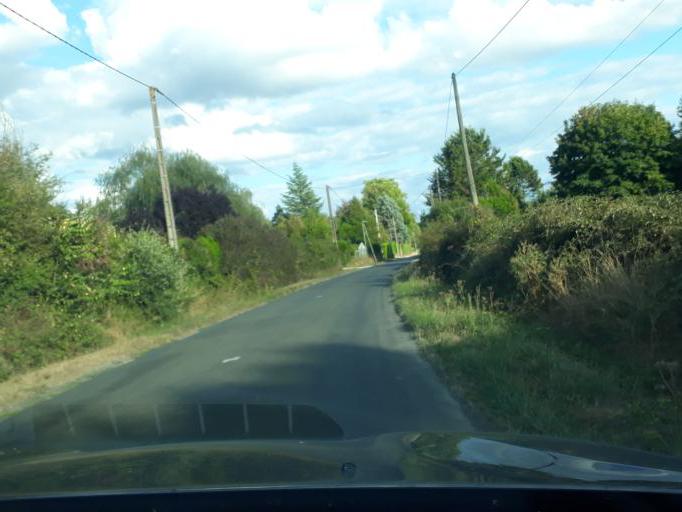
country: FR
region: Centre
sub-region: Departement du Loiret
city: Trainou
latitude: 47.9780
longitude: 2.1257
